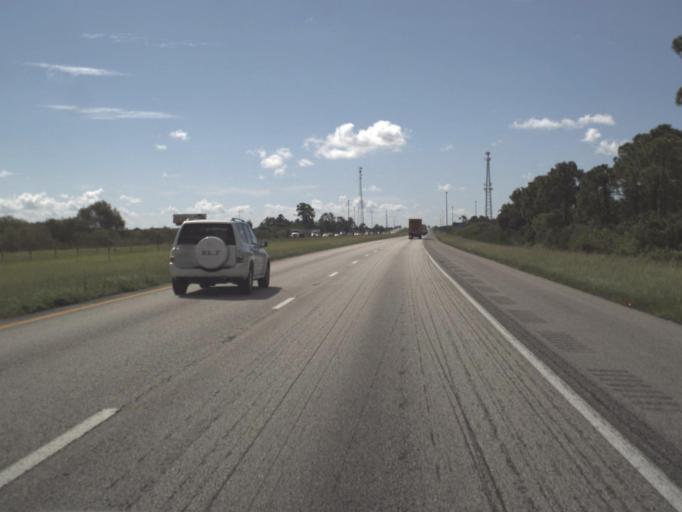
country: US
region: Florida
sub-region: Charlotte County
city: Port Charlotte
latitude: 27.0310
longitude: -82.0552
